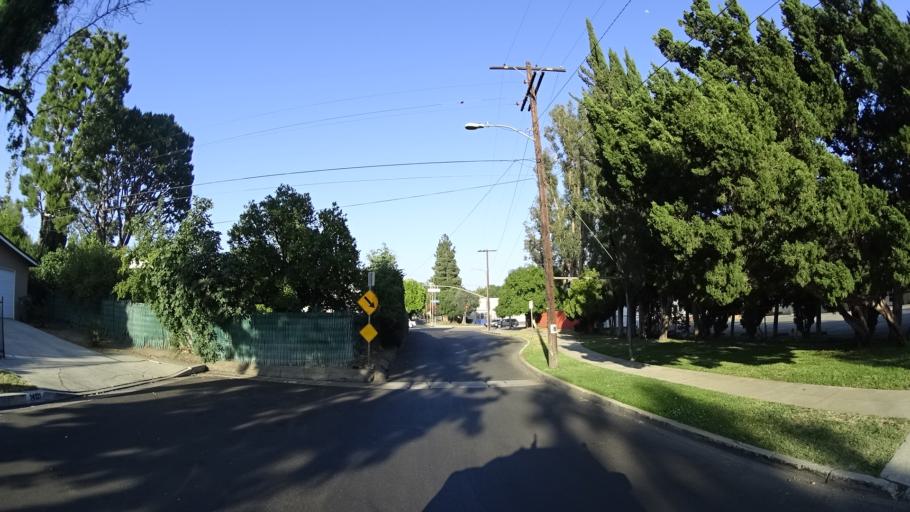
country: US
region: California
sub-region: Los Angeles County
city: Sherman Oaks
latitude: 34.1667
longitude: -118.4409
